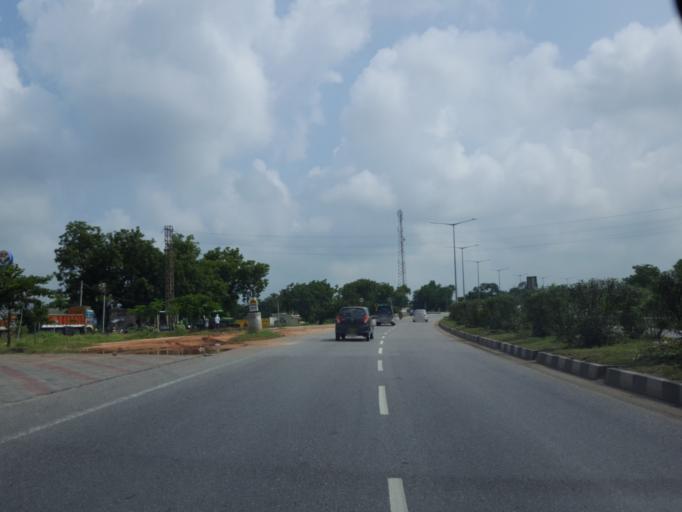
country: IN
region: Telangana
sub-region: Nalgonda
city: Bhongir
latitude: 17.2314
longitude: 78.9804
